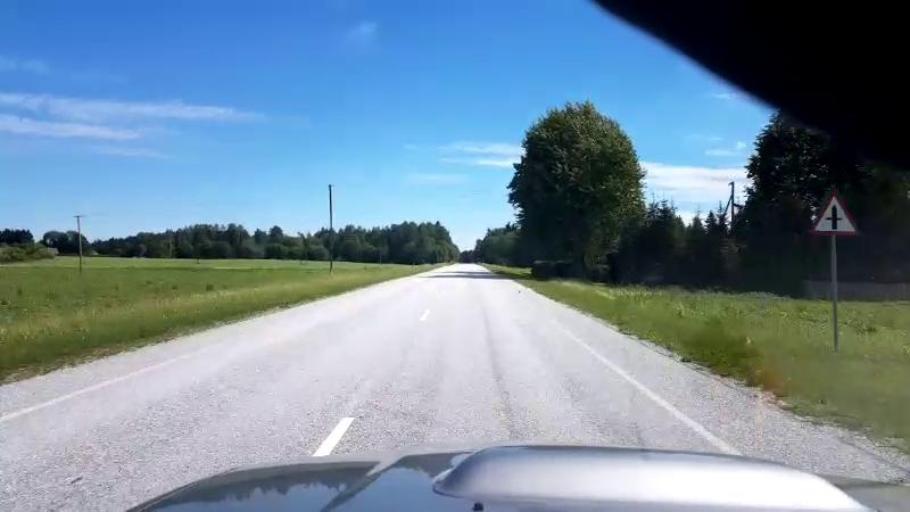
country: EE
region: Laeaene-Virumaa
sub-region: Rakke vald
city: Rakke
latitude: 58.9526
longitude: 26.1765
